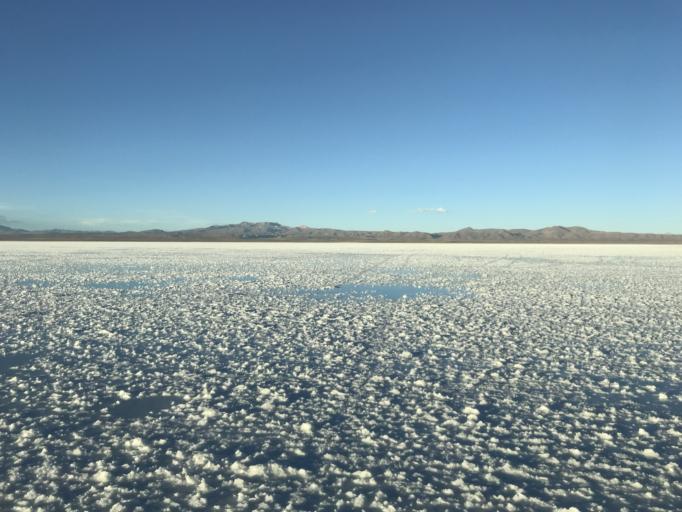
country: BO
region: Potosi
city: Colchani
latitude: -20.3847
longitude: -66.9853
